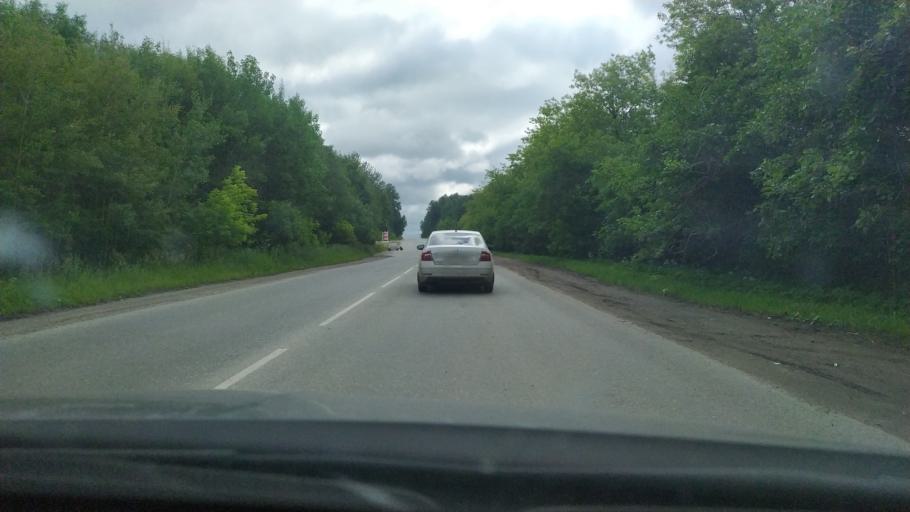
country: RU
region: Perm
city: Froly
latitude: 57.9752
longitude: 56.3260
